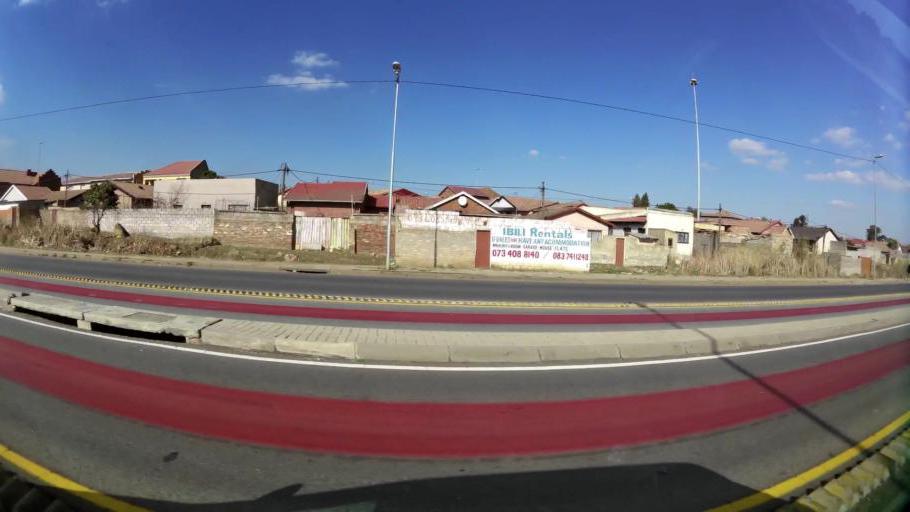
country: ZA
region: Gauteng
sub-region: City of Johannesburg Metropolitan Municipality
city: Soweto
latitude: -26.2561
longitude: 27.8927
